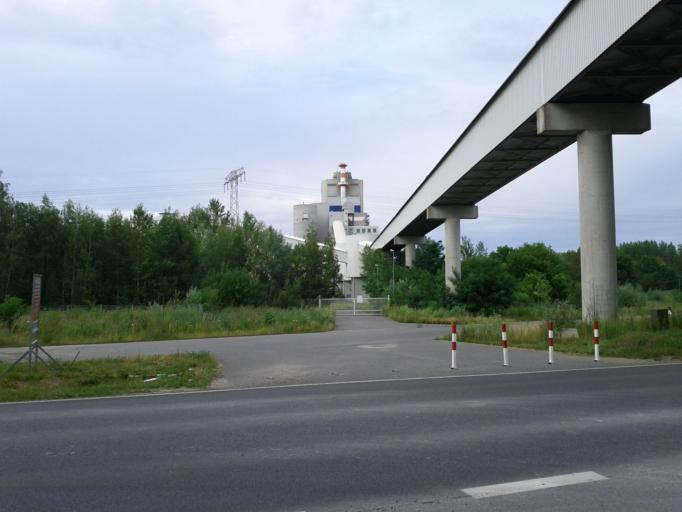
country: DE
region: Brandenburg
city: Petershagen
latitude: 52.4843
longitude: 13.8332
